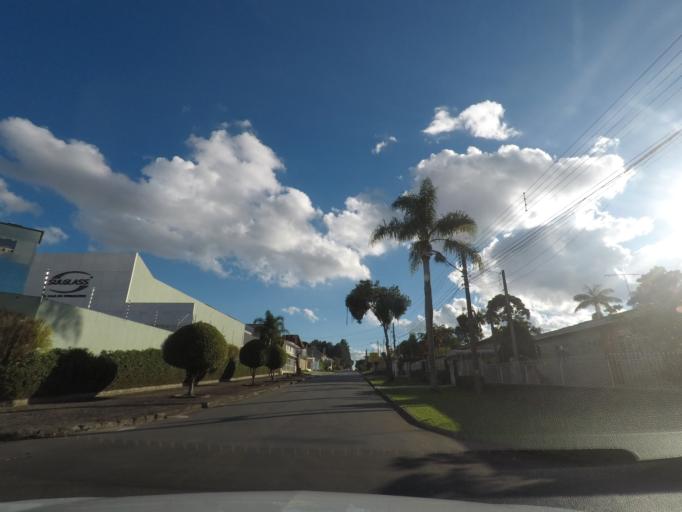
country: BR
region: Parana
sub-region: Curitiba
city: Curitiba
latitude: -25.4809
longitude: -49.2573
